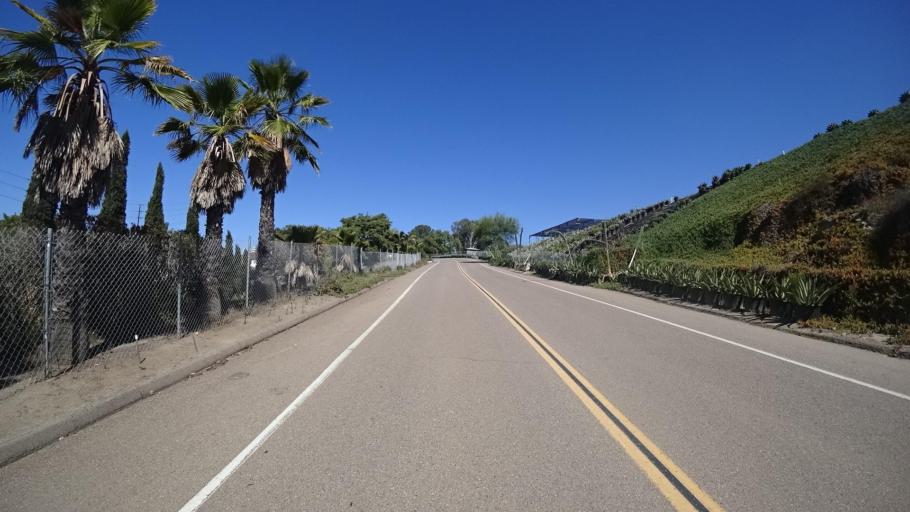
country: US
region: California
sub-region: San Diego County
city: Chula Vista
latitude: 32.6446
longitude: -117.0558
